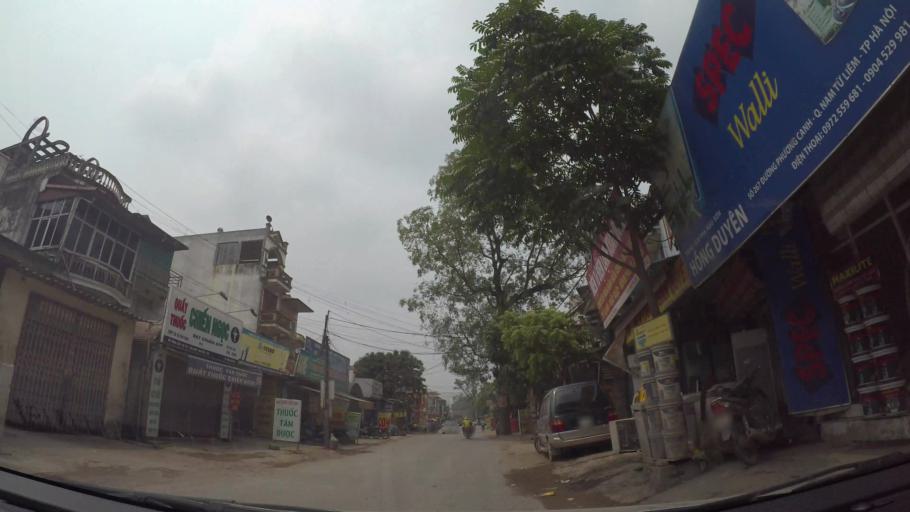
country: VN
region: Ha Noi
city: Cau Dien
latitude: 21.0338
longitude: 105.7388
